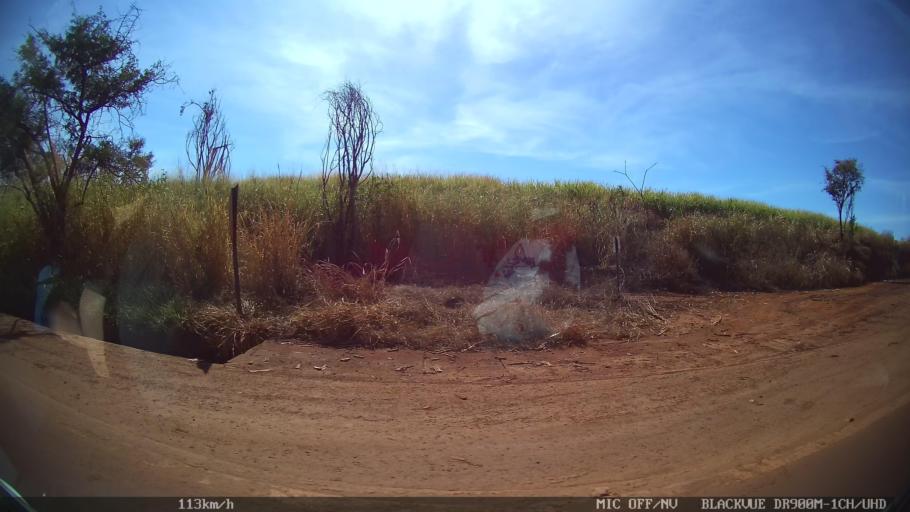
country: BR
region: Sao Paulo
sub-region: Sao Joaquim Da Barra
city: Sao Joaquim da Barra
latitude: -20.5508
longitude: -47.7429
